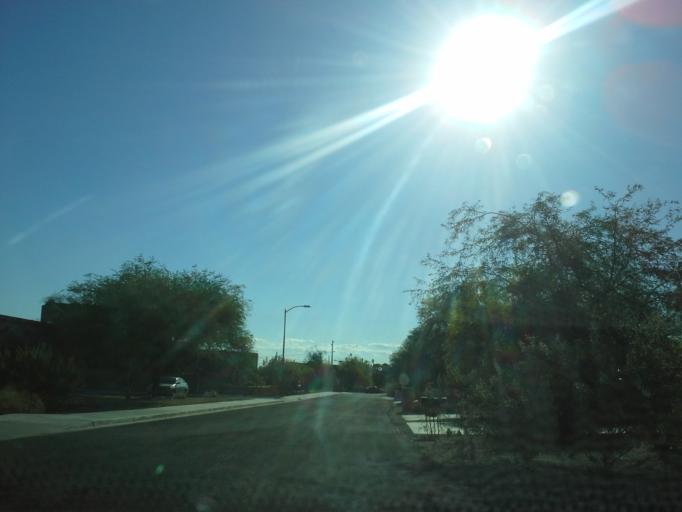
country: US
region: Arizona
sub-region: Maricopa County
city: Paradise Valley
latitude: 33.5579
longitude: -112.0463
